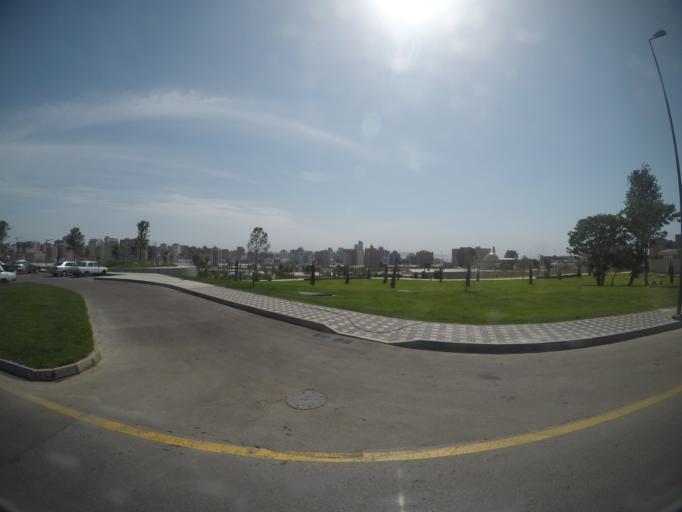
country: AZ
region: Baki
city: Badamdar
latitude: 40.3737
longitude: 49.8244
